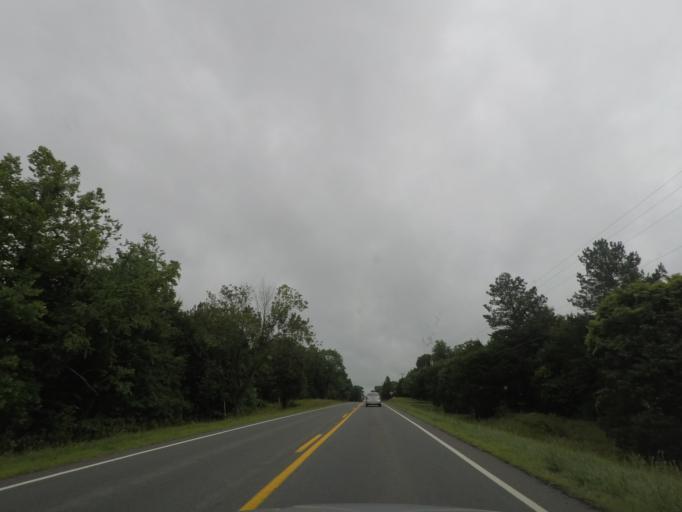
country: US
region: Virginia
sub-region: Fluvanna County
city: Palmyra
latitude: 37.8443
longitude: -78.2724
